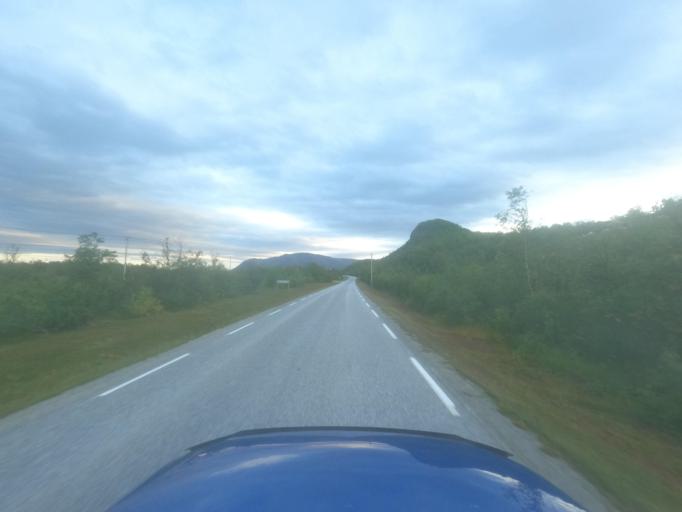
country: NO
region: Finnmark Fylke
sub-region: Porsanger
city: Lakselv
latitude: 70.1861
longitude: 24.9117
